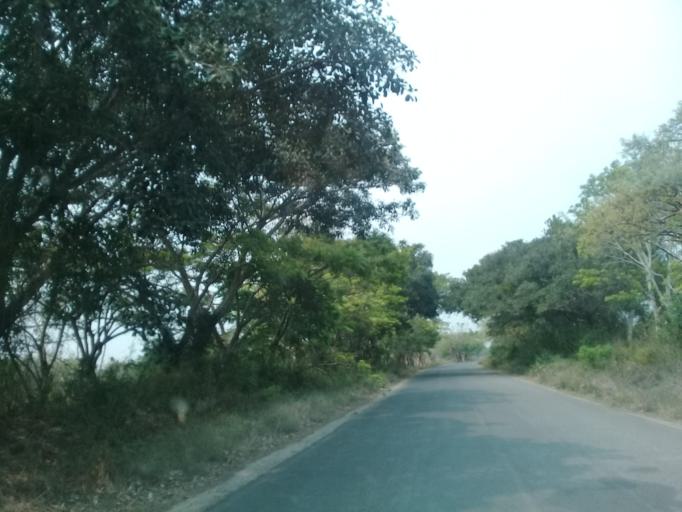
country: MX
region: Veracruz
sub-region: Medellin
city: La Laguna y Monte del Castillo
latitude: 18.9558
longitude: -96.1242
